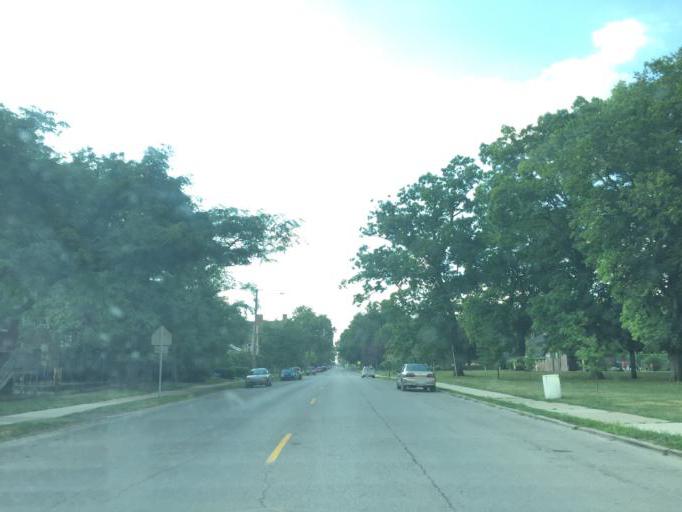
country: US
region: Michigan
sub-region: Wayne County
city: Detroit
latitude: 42.3170
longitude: -83.0934
